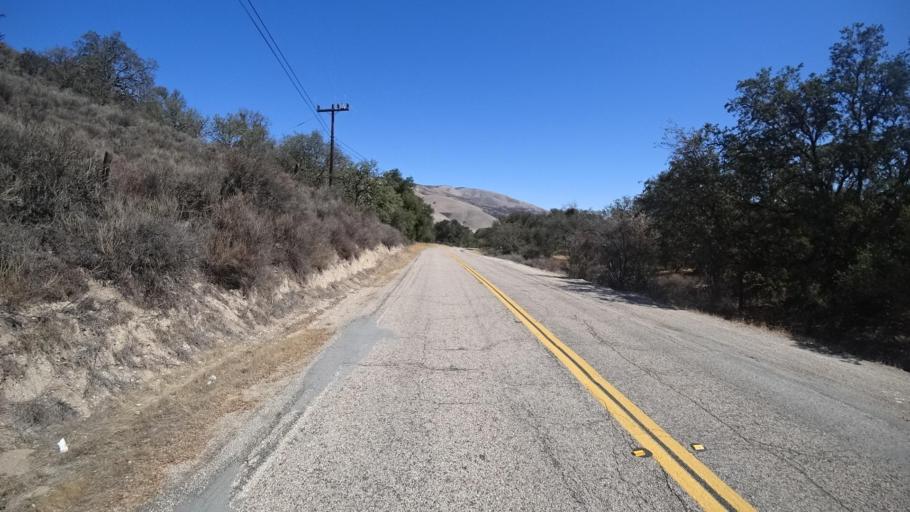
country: US
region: California
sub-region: Monterey County
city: Greenfield
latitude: 36.2643
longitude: -121.4132
